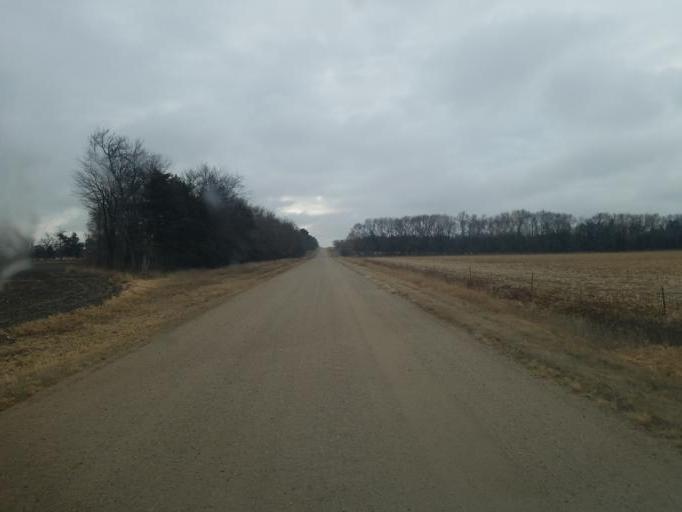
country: US
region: Nebraska
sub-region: Pierce County
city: Plainview
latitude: 42.4327
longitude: -97.7960
